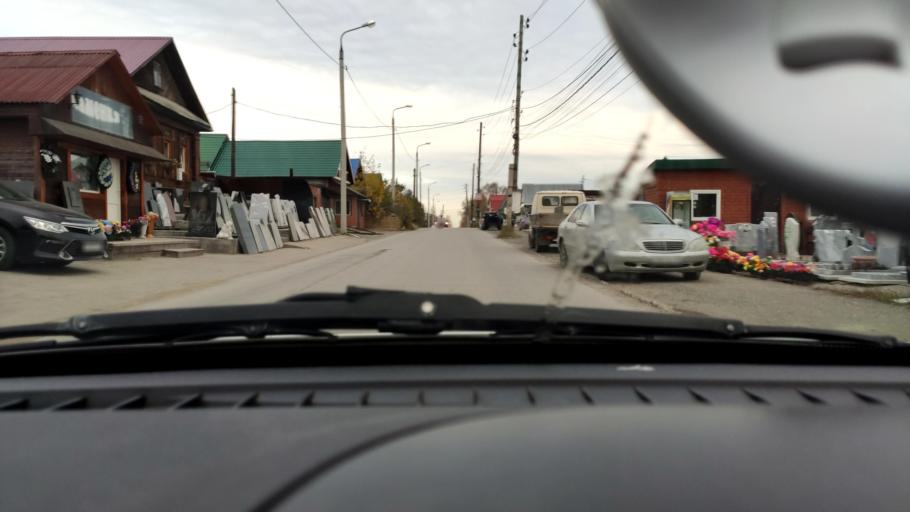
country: RU
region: Perm
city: Kondratovo
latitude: 58.0555
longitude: 56.1228
